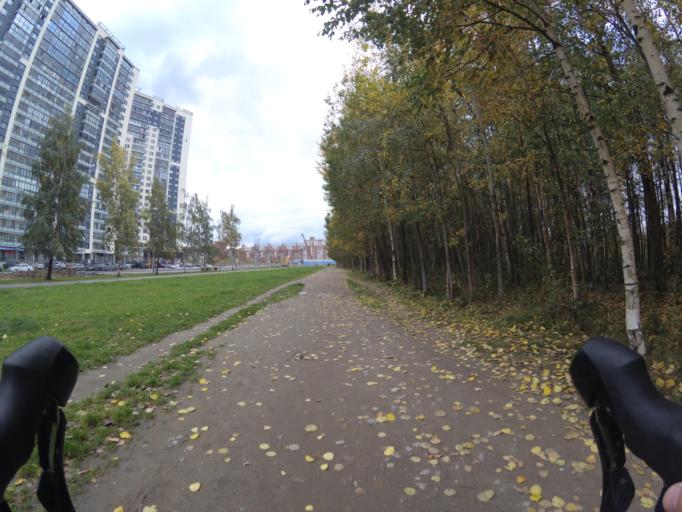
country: RU
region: Leningrad
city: Untolovo
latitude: 59.9950
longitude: 30.1919
